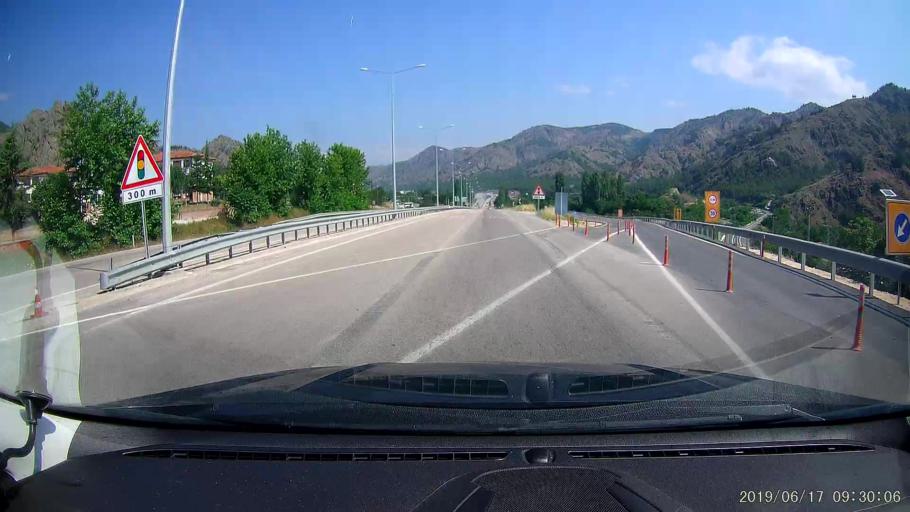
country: TR
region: Amasya
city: Amasya
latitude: 40.7024
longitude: 35.8056
